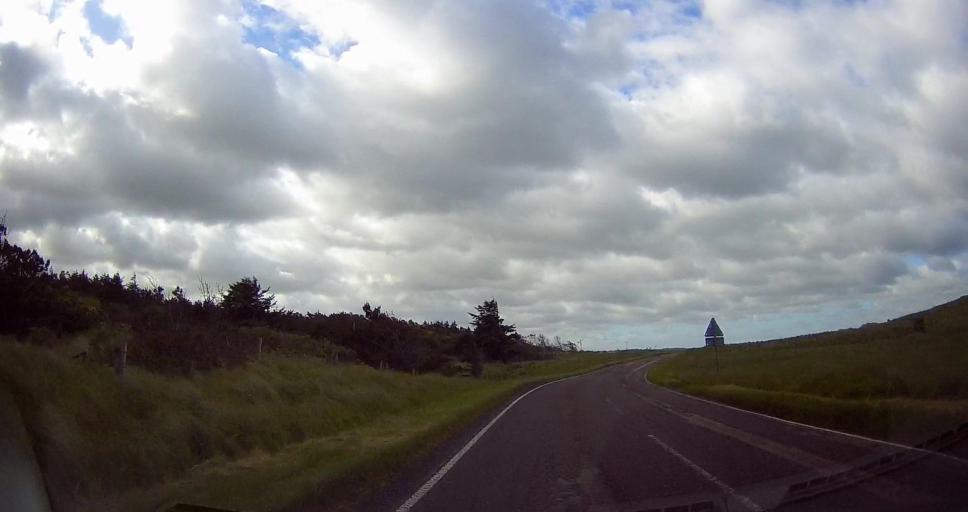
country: GB
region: Scotland
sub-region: Highland
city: Thurso
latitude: 58.6121
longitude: -3.3433
